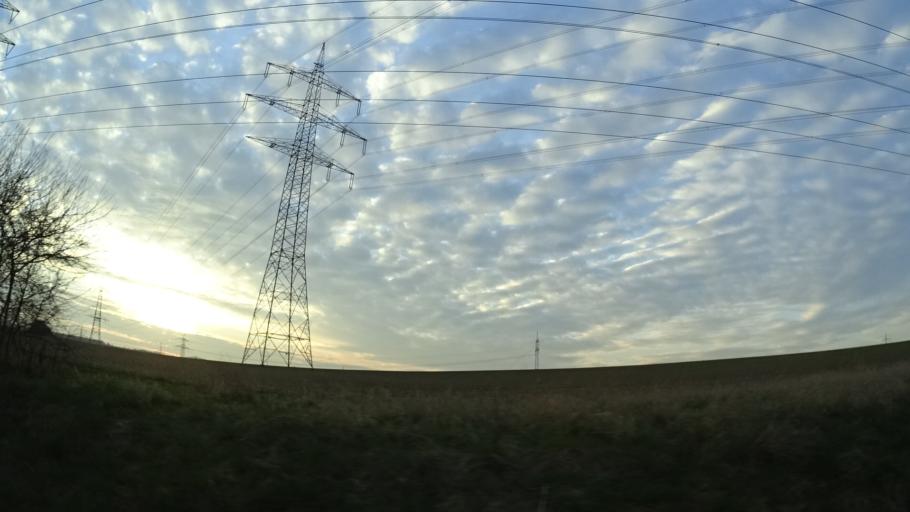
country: DE
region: Baden-Wuerttemberg
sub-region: Regierungsbezirk Stuttgart
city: Markgroningen
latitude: 48.9075
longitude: 9.0559
